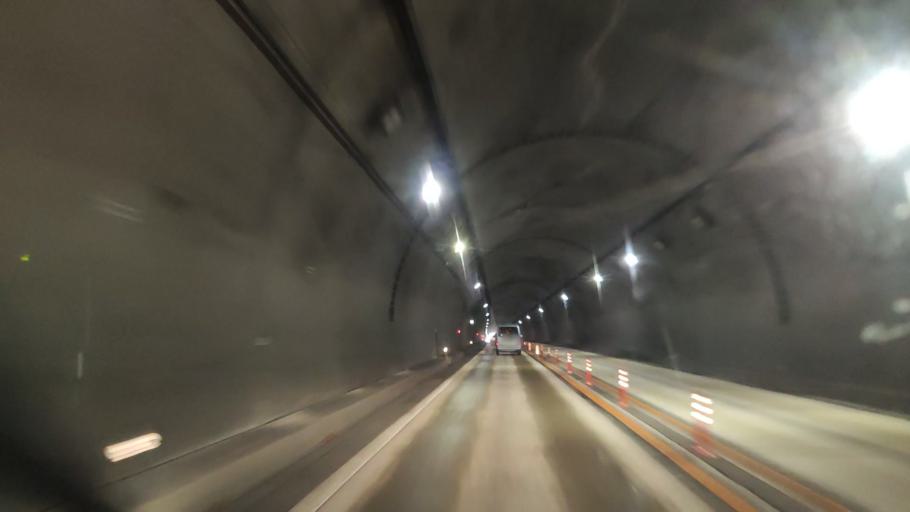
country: JP
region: Tokushima
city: Kamojimacho-jogejima
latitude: 34.1129
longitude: 134.3213
